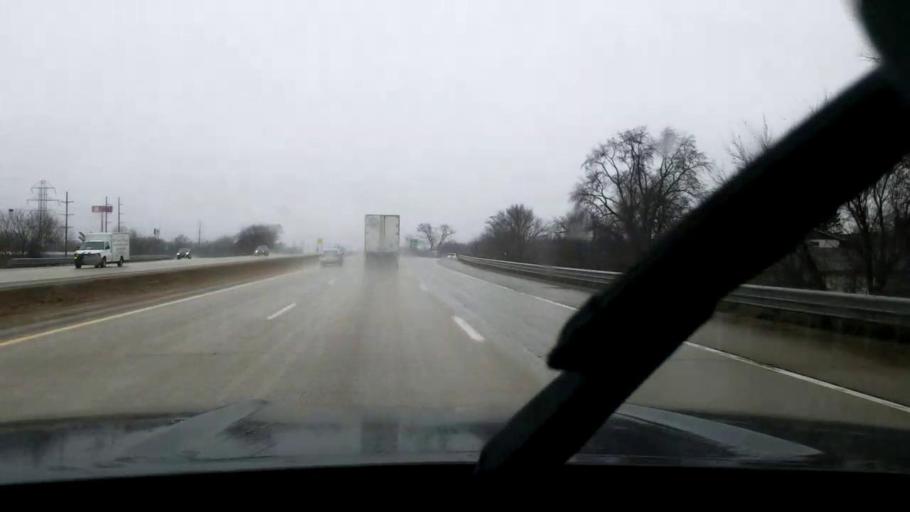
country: US
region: Michigan
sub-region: Jackson County
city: Michigan Center
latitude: 42.2545
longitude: -84.3566
